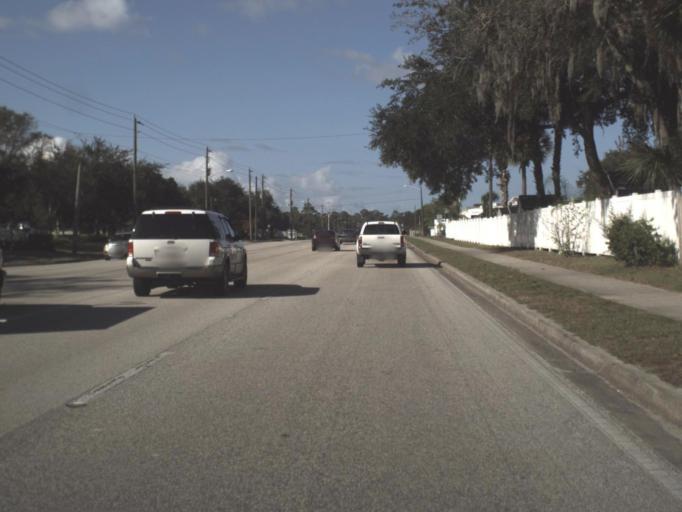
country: US
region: Florida
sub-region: Volusia County
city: Port Orange
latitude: 29.1320
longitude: -81.0277
